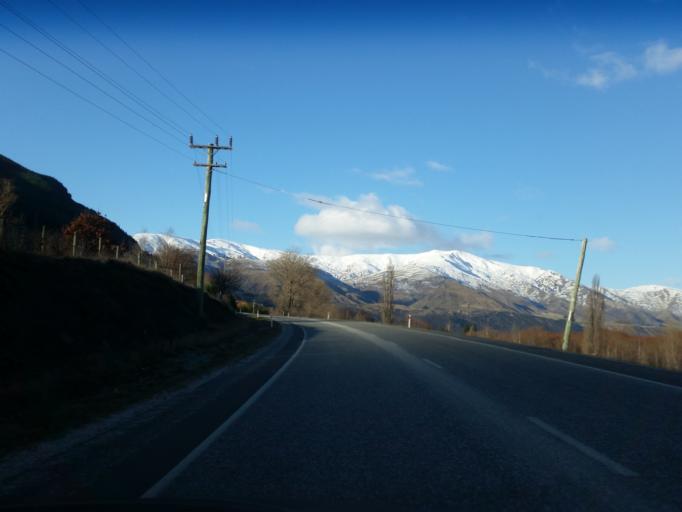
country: NZ
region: Otago
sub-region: Queenstown-Lakes District
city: Arrowtown
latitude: -44.9468
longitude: 168.7839
